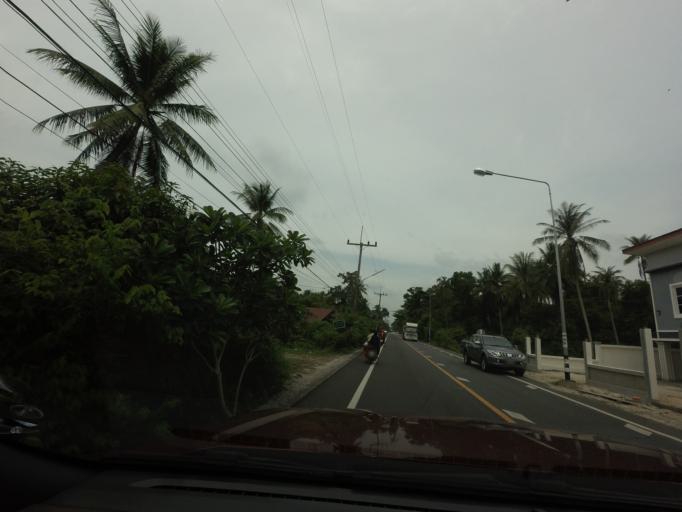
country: TH
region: Pattani
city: Yaring
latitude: 6.8564
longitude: 101.3617
